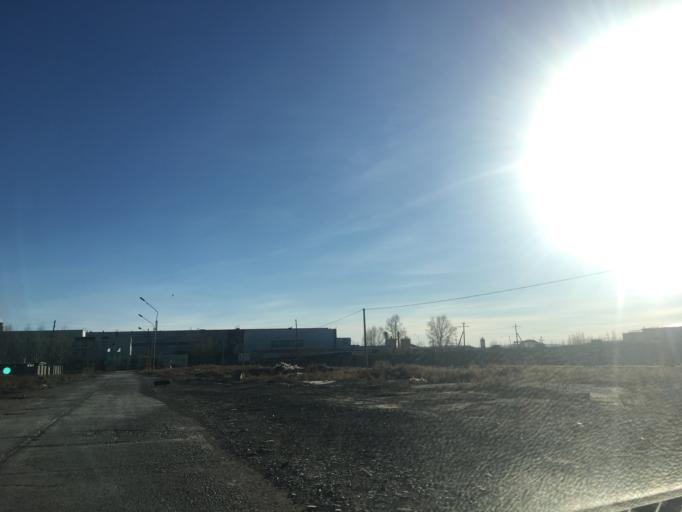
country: MN
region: Ulaanbaatar
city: Ulaanbaatar
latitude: 47.9004
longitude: 106.7969
